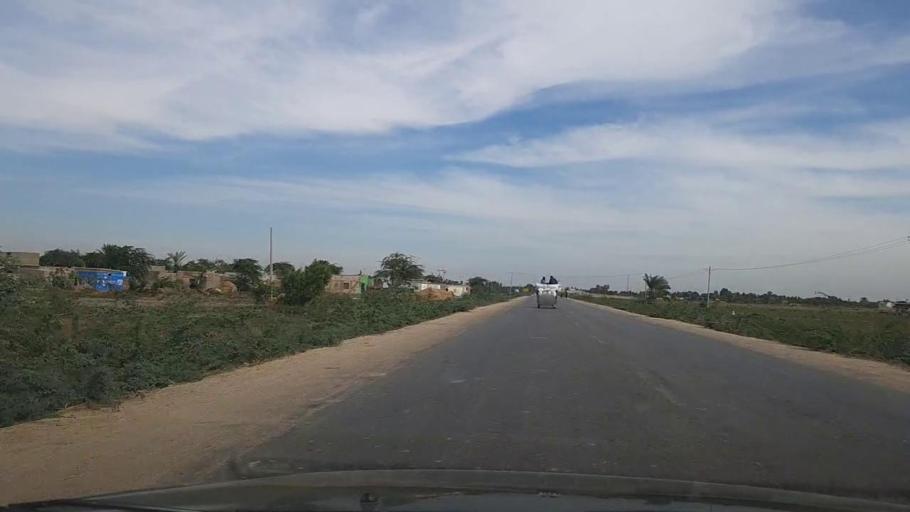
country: PK
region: Sindh
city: Thatta
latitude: 24.7788
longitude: 67.9468
